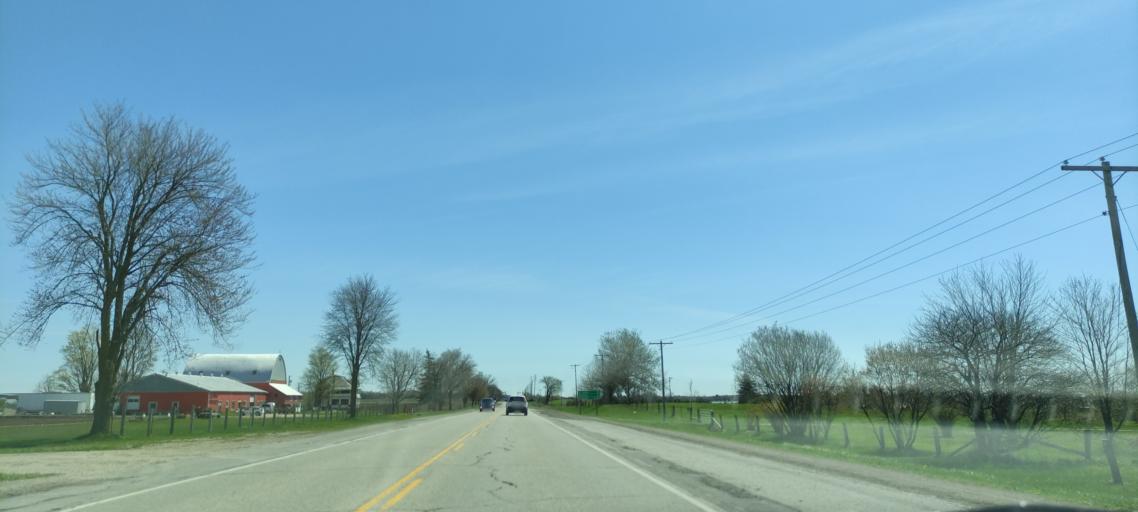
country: CA
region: Ontario
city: Waterloo
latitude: 43.5957
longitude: -80.5155
